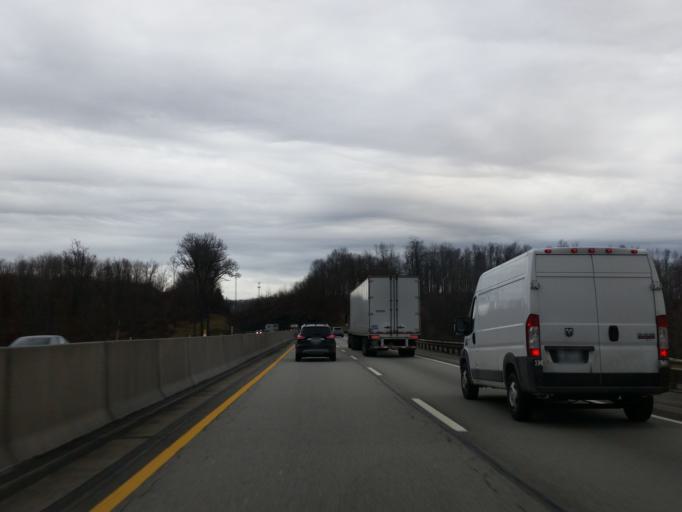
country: US
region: Pennsylvania
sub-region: Somerset County
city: Somerset
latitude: 40.0713
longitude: -79.1593
